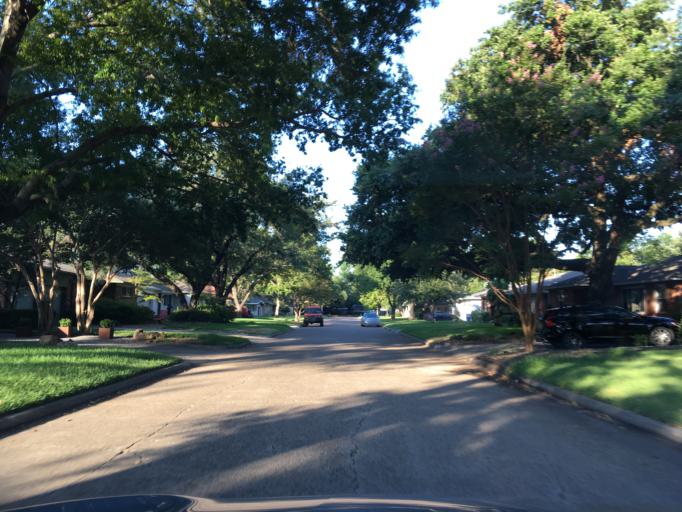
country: US
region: Texas
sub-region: Dallas County
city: Highland Park
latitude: 32.8565
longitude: -96.7360
